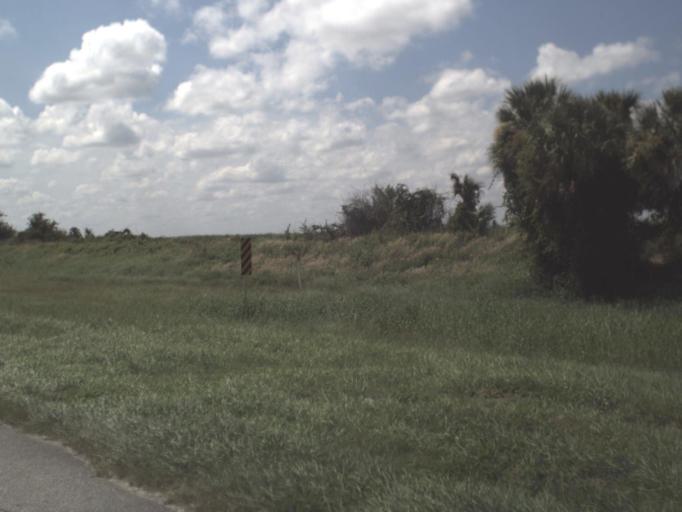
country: US
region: Florida
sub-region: Hendry County
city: Port LaBelle
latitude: 26.6060
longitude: -81.4366
